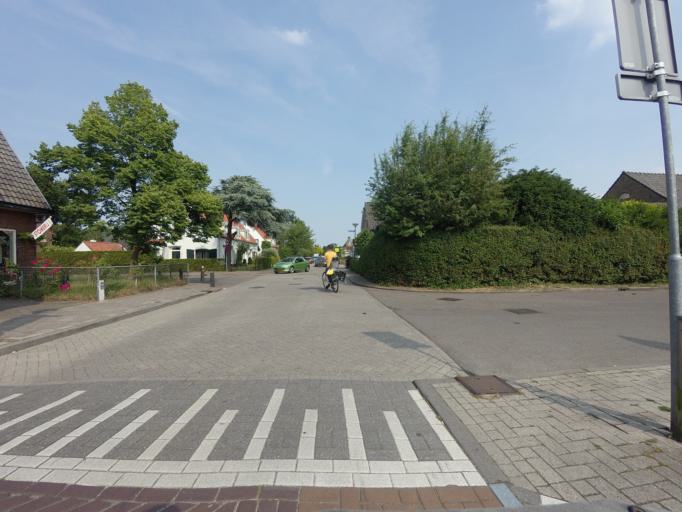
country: NL
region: North Holland
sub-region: Gemeente Wijdemeren
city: Nieuw-Loosdrecht
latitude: 52.1996
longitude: 5.1405
